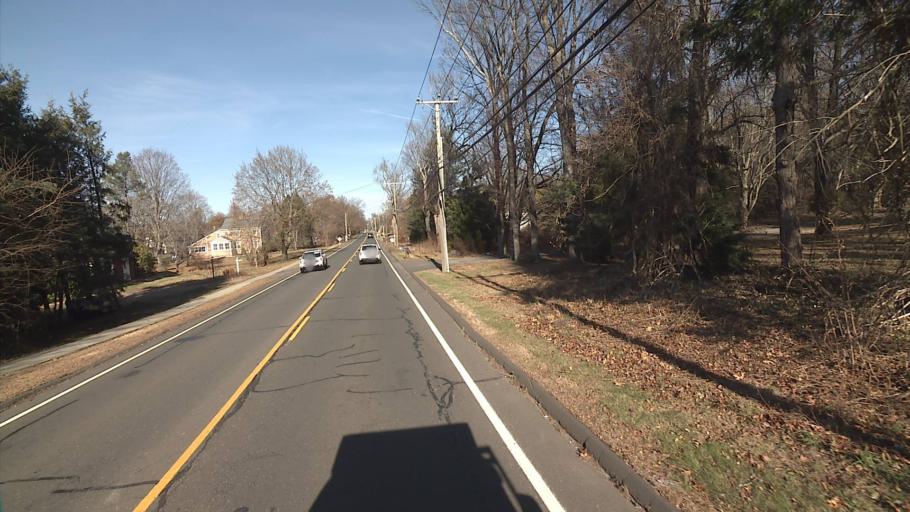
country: US
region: Connecticut
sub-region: Hartford County
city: Glastonbury Center
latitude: 41.6413
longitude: -72.6059
